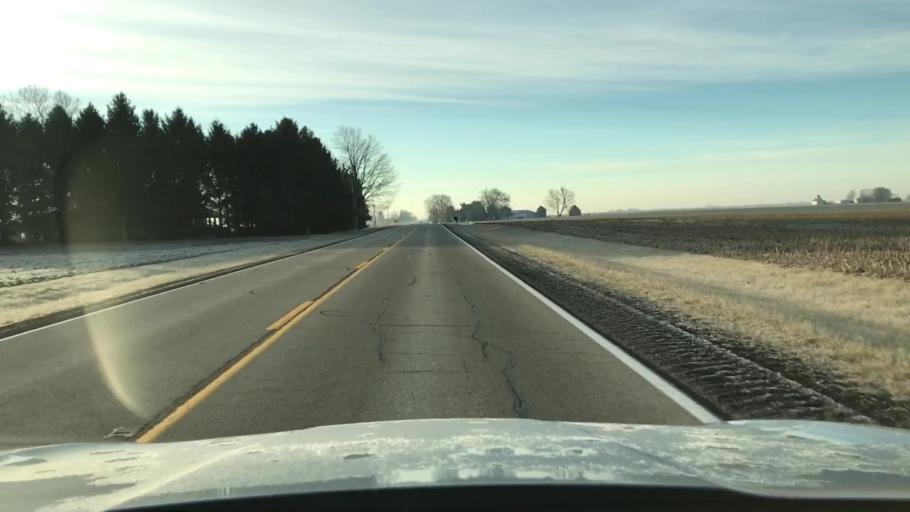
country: US
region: Illinois
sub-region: McLean County
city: Hudson
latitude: 40.6150
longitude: -88.9455
